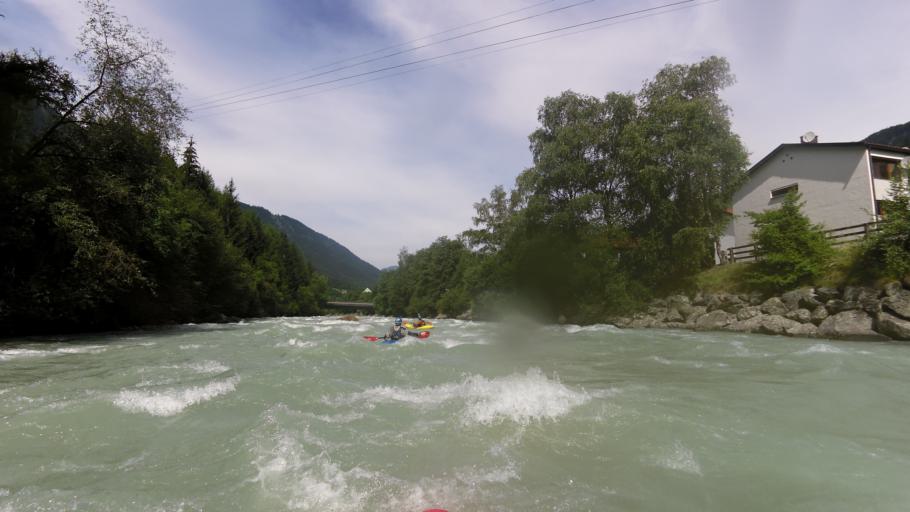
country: AT
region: Tyrol
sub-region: Politischer Bezirk Imst
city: Oetz
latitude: 47.2021
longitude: 10.8948
